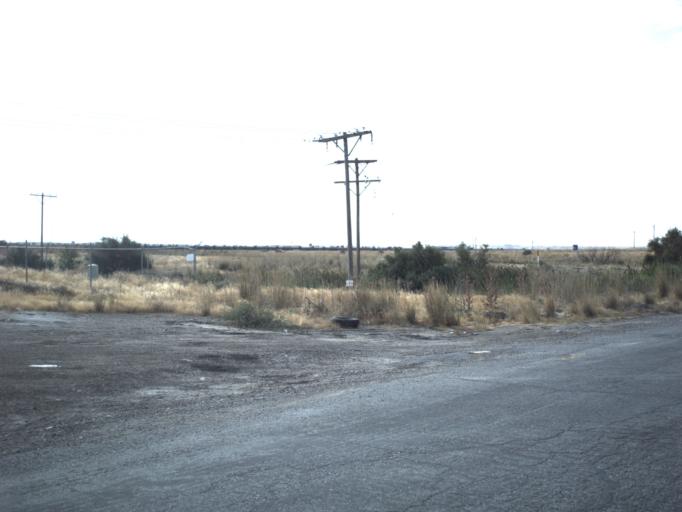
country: US
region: Utah
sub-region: Salt Lake County
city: Magna
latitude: 40.7740
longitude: -112.0632
